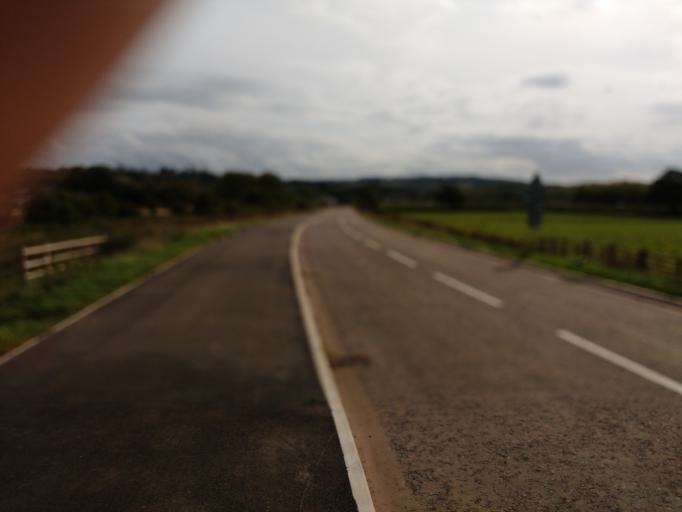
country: GB
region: England
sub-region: North Somerset
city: Long Ashton
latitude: 51.4344
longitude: -2.6341
